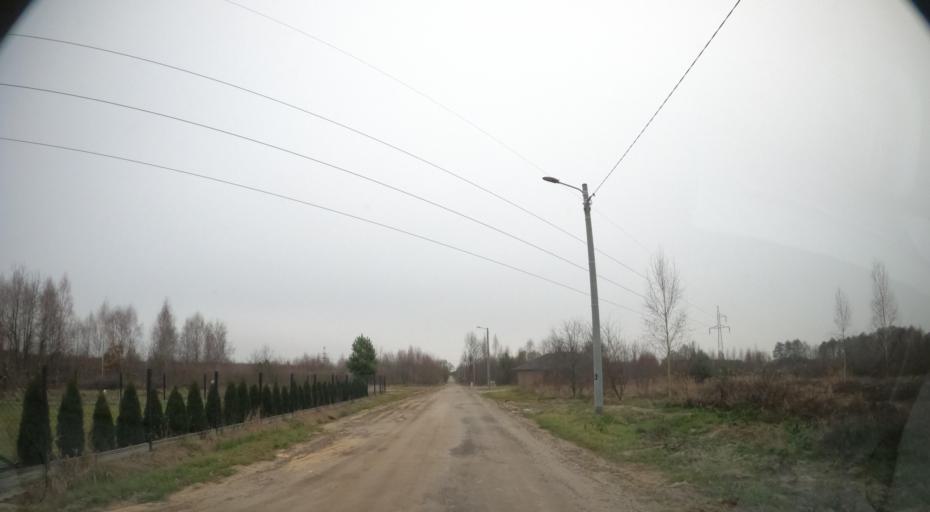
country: PL
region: Masovian Voivodeship
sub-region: Powiat radomski
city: Jastrzebia
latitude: 51.4862
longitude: 21.1893
